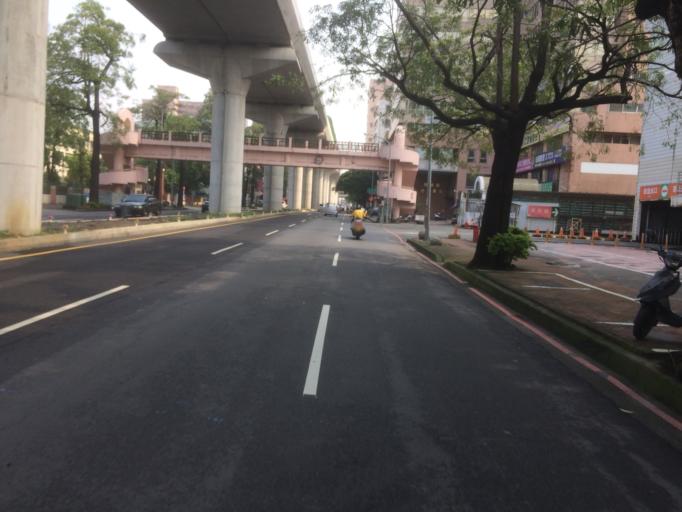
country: TW
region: Taiwan
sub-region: Taichung City
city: Taichung
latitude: 24.1767
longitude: 120.6997
